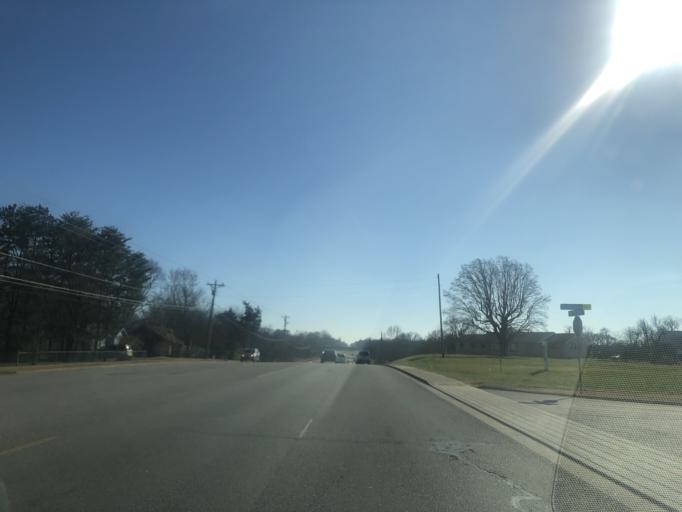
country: US
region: Tennessee
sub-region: Rutherford County
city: Smyrna
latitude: 35.9572
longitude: -86.5180
